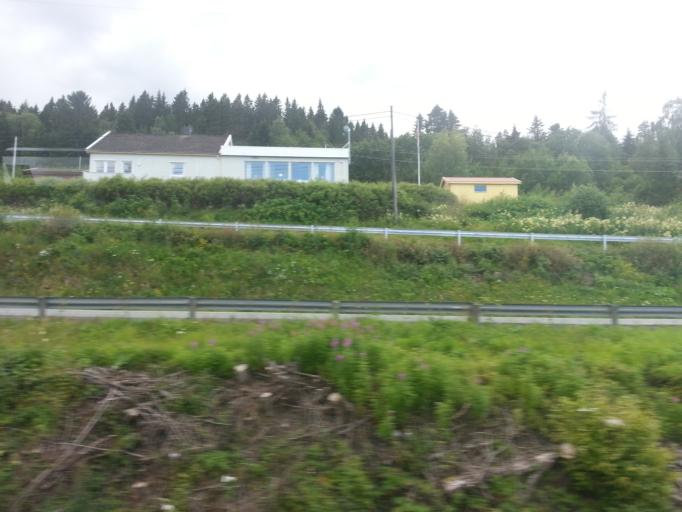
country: NO
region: Sor-Trondelag
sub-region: Malvik
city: Hommelvik
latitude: 63.4293
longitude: 10.7691
